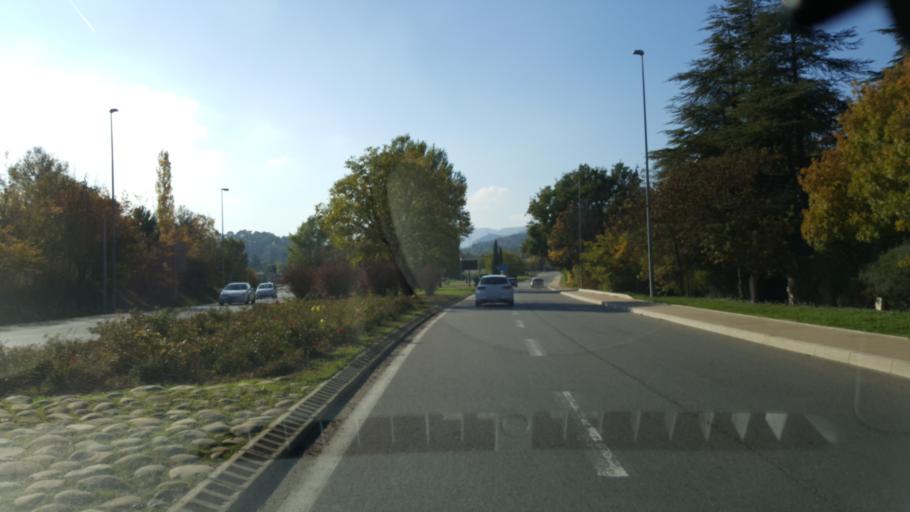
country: FR
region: Provence-Alpes-Cote d'Azur
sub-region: Departement des Bouches-du-Rhone
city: Auriol
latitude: 43.3680
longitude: 5.6473
